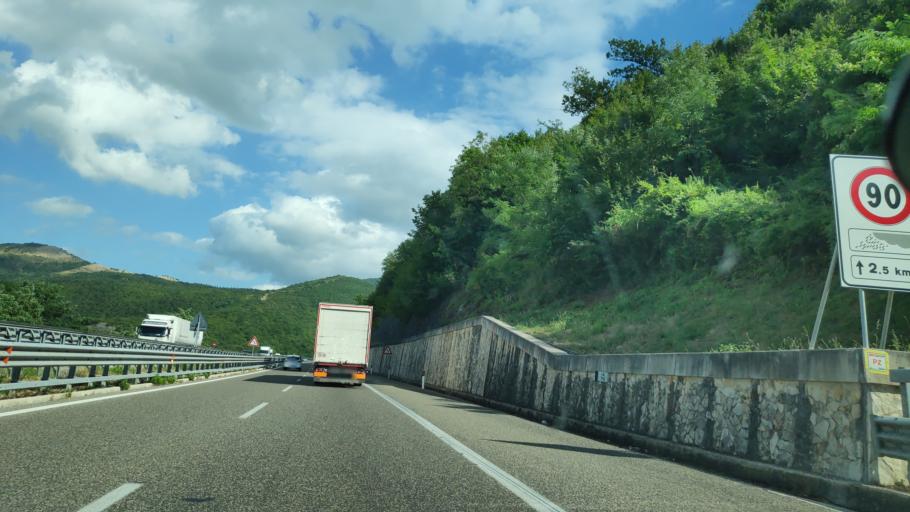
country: IT
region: Campania
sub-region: Provincia di Salerno
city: Pertosa
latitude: 40.5326
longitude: 15.4252
